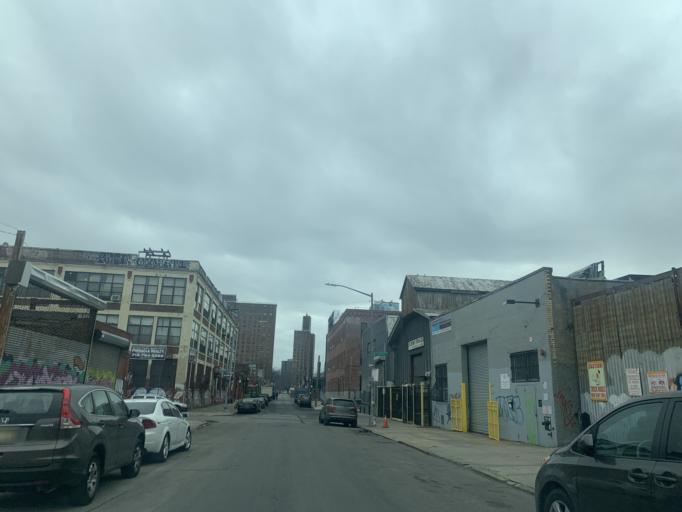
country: US
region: New York
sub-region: Queens County
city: Long Island City
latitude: 40.7034
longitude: -73.9338
